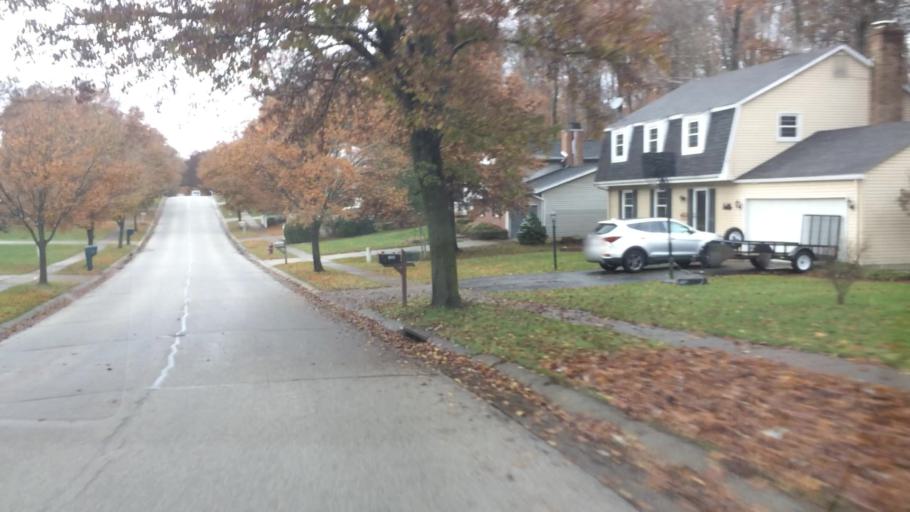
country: US
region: Ohio
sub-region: Summit County
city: Silver Lake
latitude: 41.1783
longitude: -81.4612
